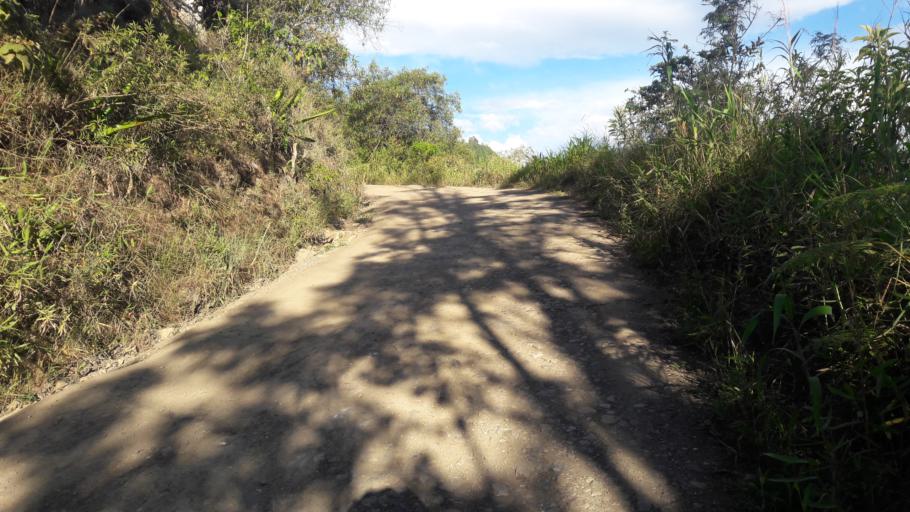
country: CO
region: Cundinamarca
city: Tenza
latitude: 5.0895
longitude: -73.4275
